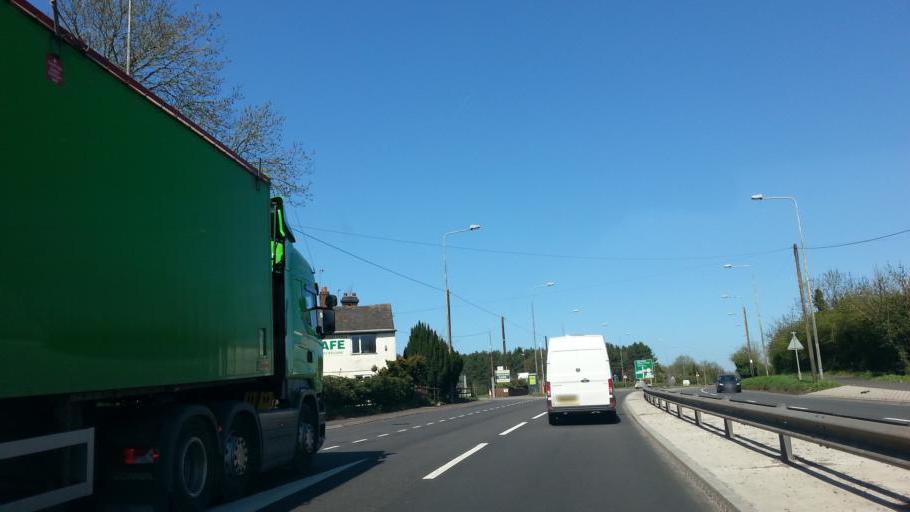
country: GB
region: England
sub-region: Staffordshire
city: Brewood
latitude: 52.6689
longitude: -2.1320
